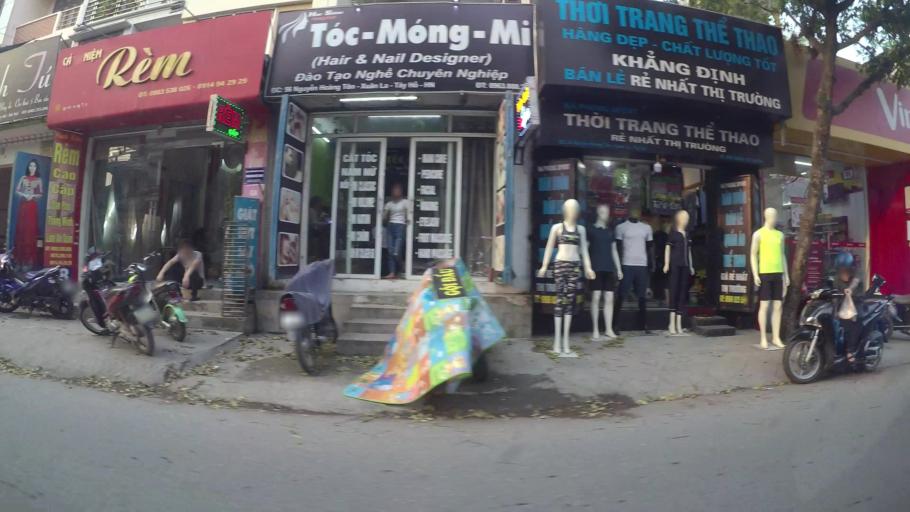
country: VN
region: Ha Noi
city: Tay Ho
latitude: 21.0716
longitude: 105.8063
